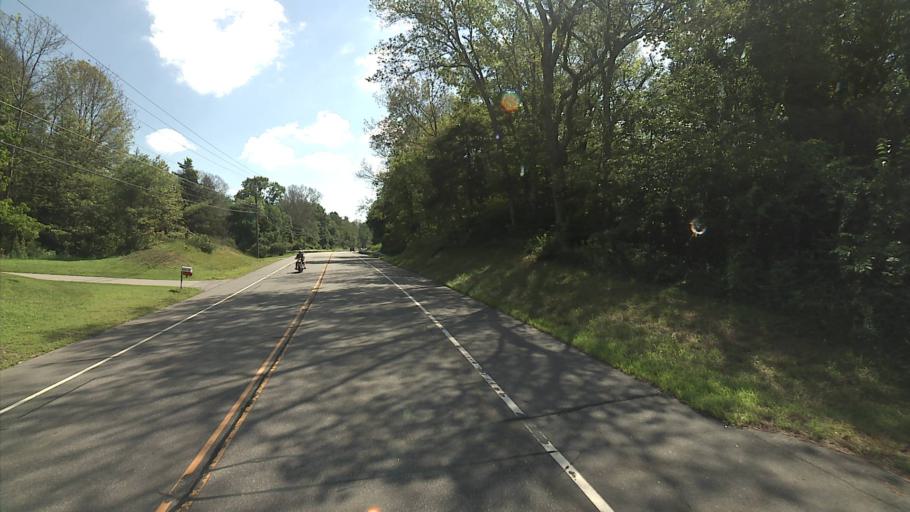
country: US
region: Connecticut
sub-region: Windham County
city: Plainfield Village
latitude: 41.6966
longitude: -71.9839
